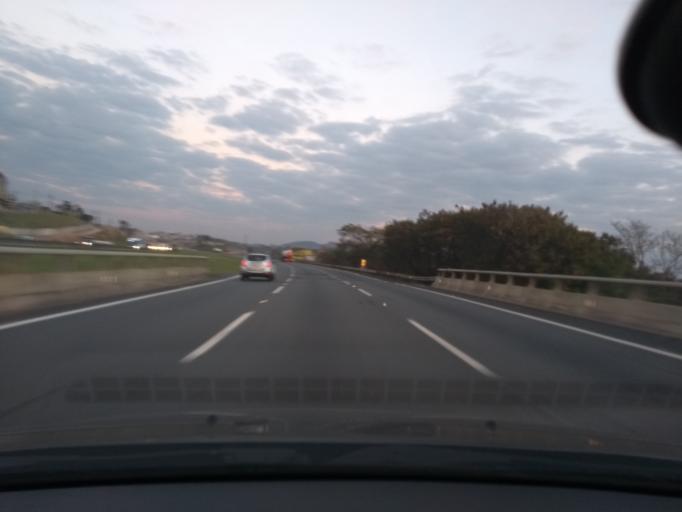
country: BR
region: Sao Paulo
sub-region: Louveira
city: Louveira
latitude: -23.1366
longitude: -46.9786
